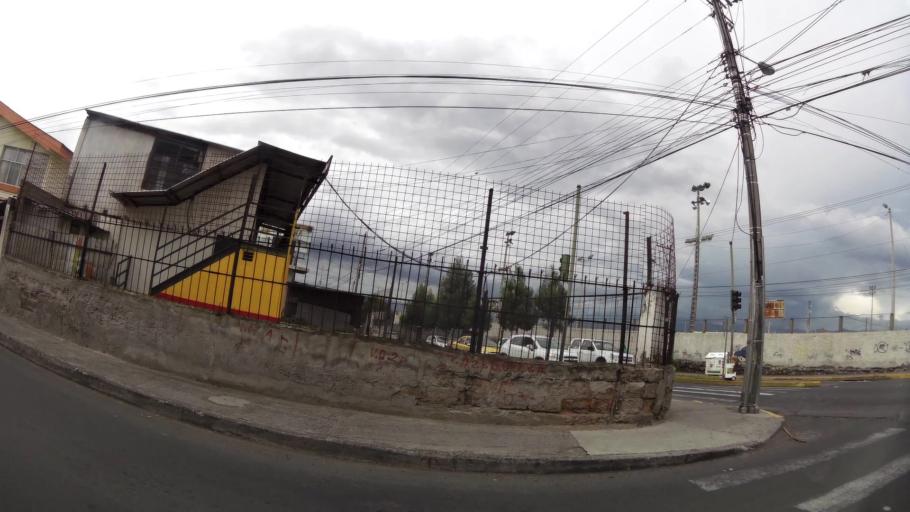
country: EC
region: Tungurahua
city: Ambato
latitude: -1.2721
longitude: -78.6296
